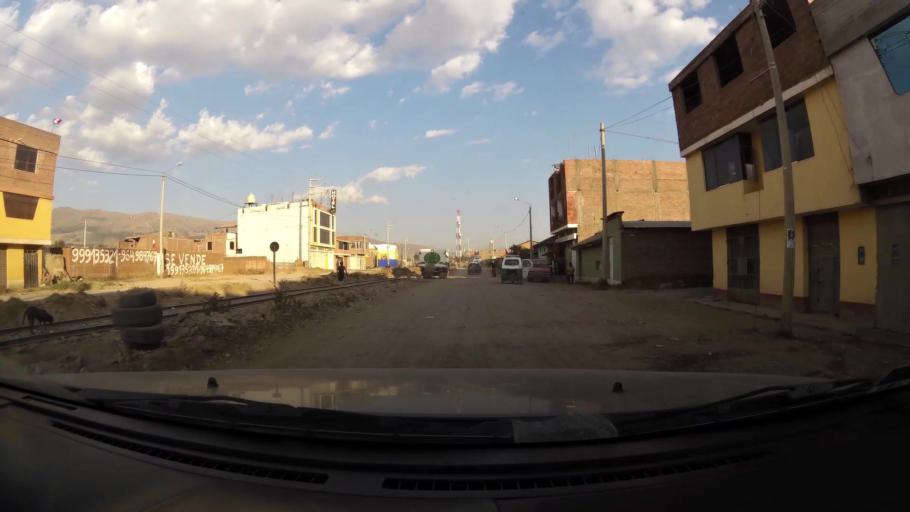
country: PE
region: Junin
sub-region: Provincia de Huancayo
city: Pilcomay
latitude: -12.0368
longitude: -75.2273
